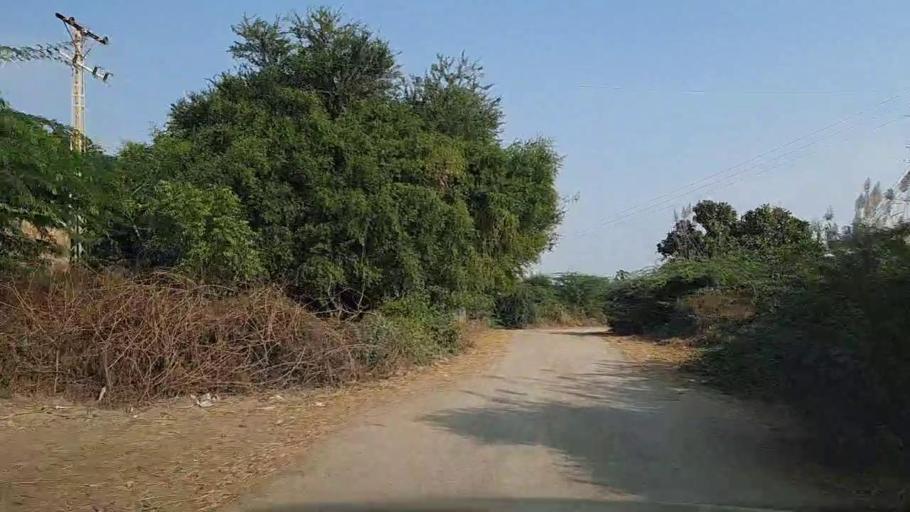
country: PK
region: Sindh
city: Thatta
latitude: 24.6513
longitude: 67.9230
